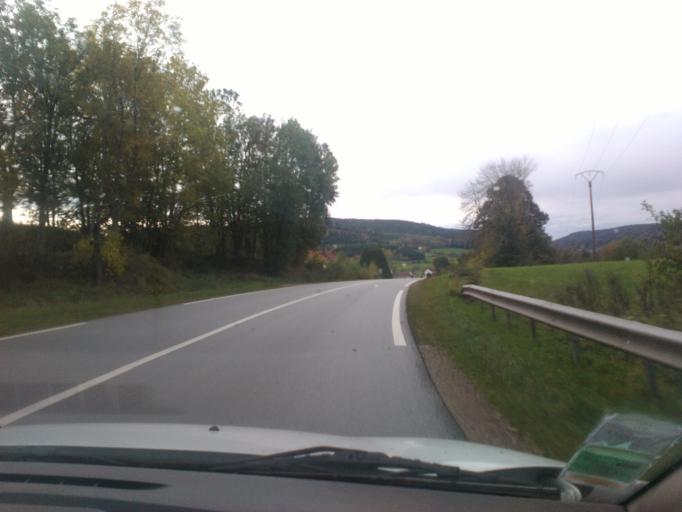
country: FR
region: Lorraine
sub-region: Departement des Vosges
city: Anould
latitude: 48.1581
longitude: 6.9216
